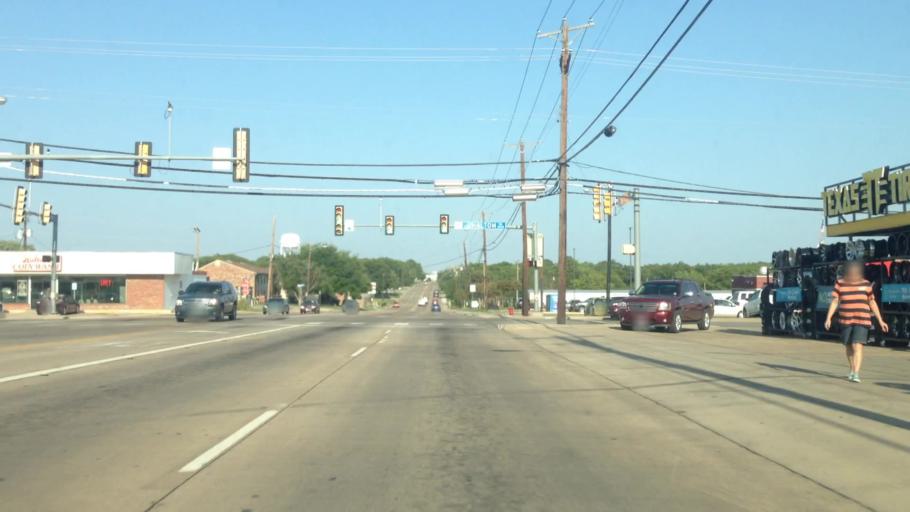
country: US
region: Texas
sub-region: Tarrant County
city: Haltom City
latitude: 32.8096
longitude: -97.2737
